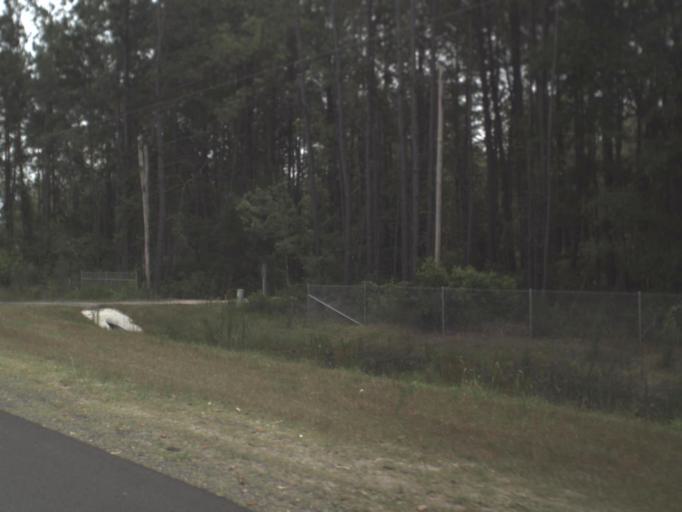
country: US
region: Florida
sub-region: Nassau County
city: Nassau Village-Ratliff
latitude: 30.4578
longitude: -81.9128
